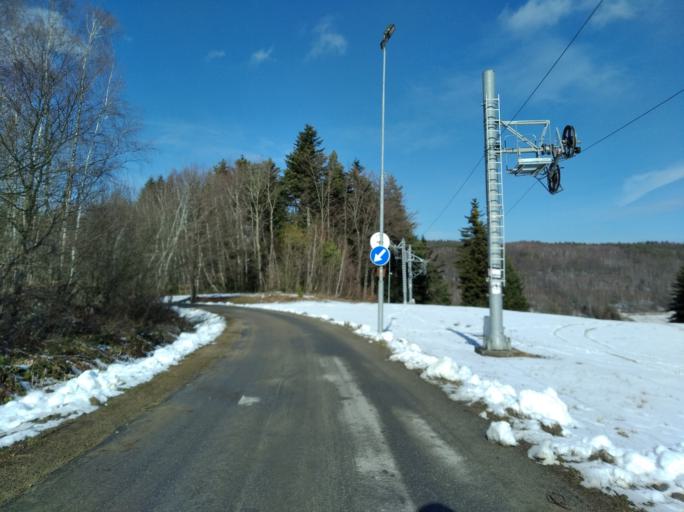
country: PL
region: Subcarpathian Voivodeship
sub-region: Powiat krosnienski
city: Korczyna
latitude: 49.7402
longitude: 21.8325
